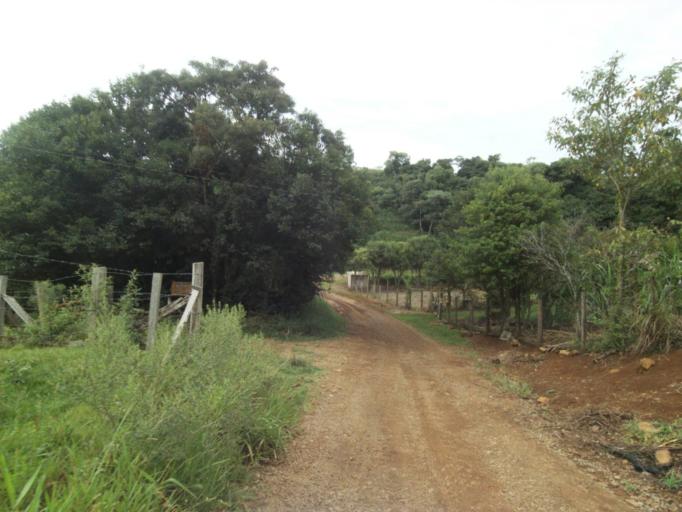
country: BR
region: Parana
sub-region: Pitanga
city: Pitanga
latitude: -24.8956
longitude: -51.9647
